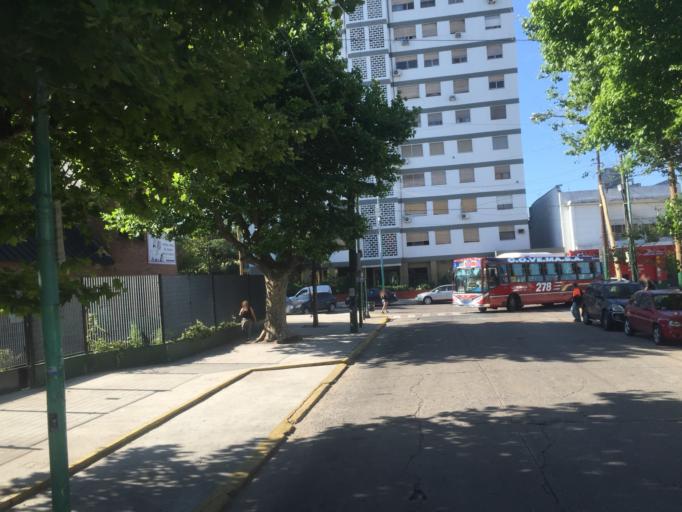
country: AR
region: Buenos Aires
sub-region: Partido de Lomas de Zamora
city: Lomas de Zamora
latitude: -34.7750
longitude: -58.3957
